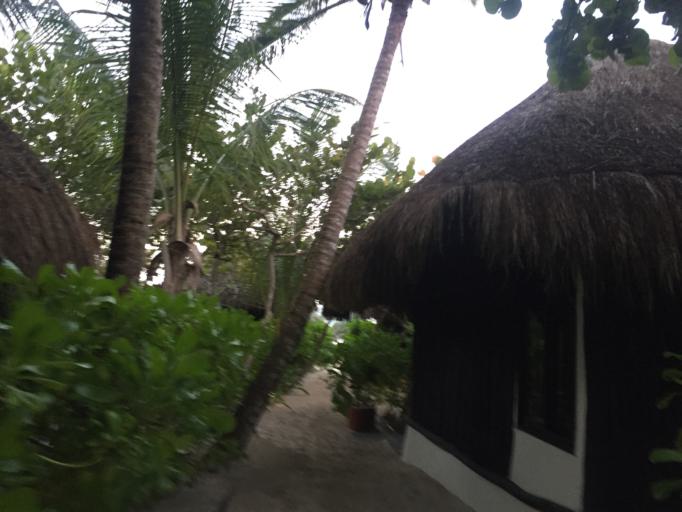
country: MX
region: Quintana Roo
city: Tulum
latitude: 20.1637
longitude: -87.4532
